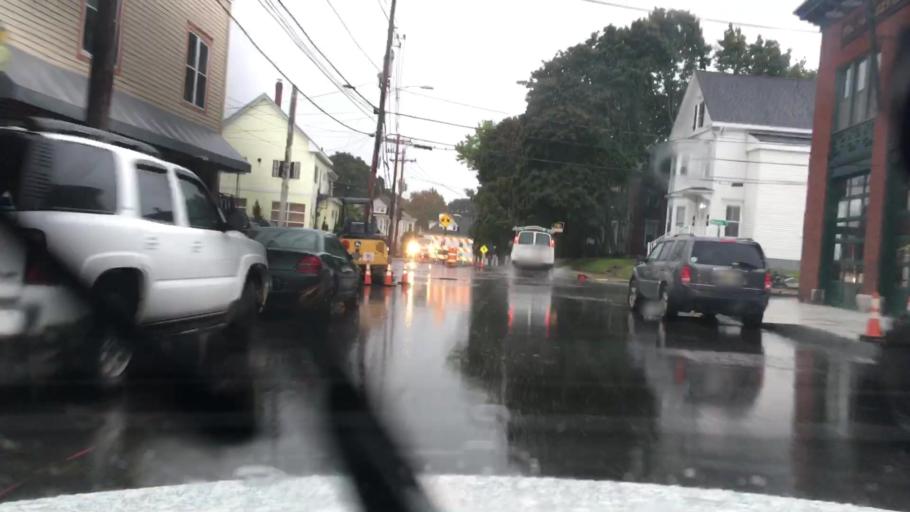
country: US
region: Maine
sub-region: Cumberland County
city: Portland
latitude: 43.6704
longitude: -70.2844
